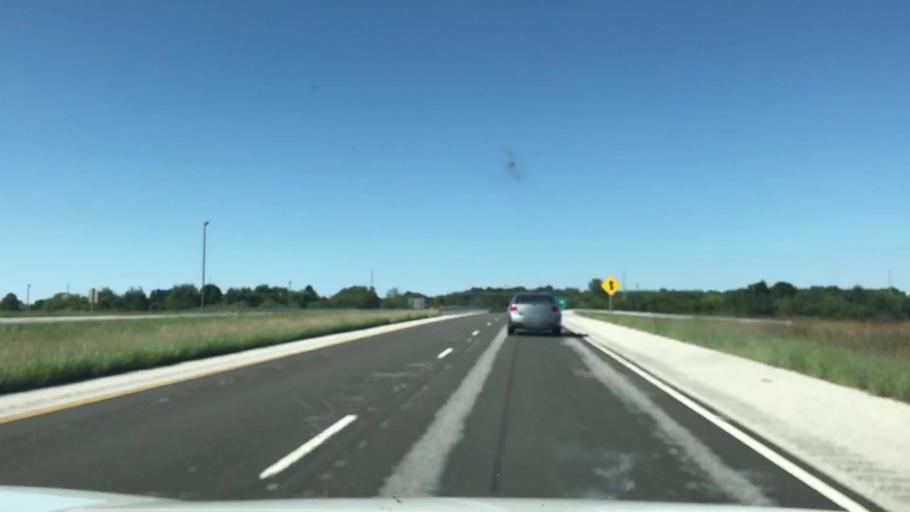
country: US
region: Illinois
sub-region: Madison County
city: South Roxana
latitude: 38.8313
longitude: -90.0435
